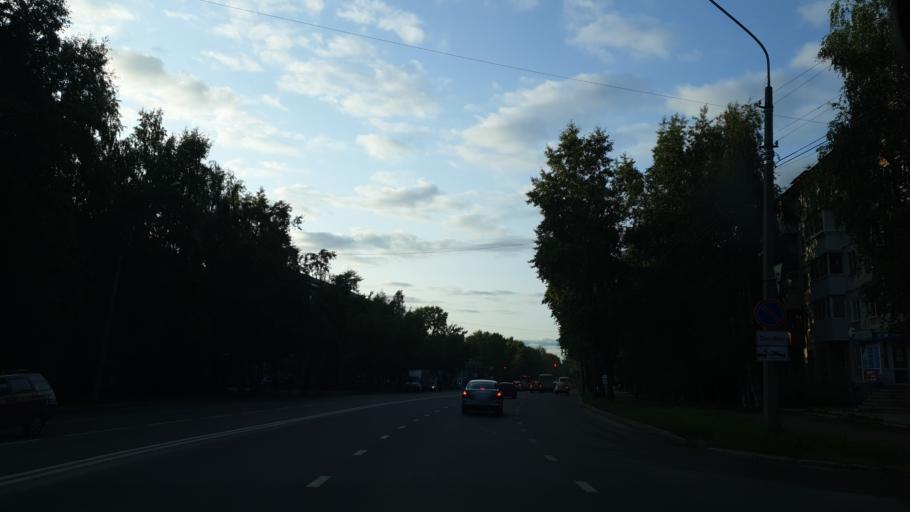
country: RU
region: Komi Republic
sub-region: Syktyvdinskiy Rayon
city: Syktyvkar
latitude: 61.6675
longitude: 50.8125
